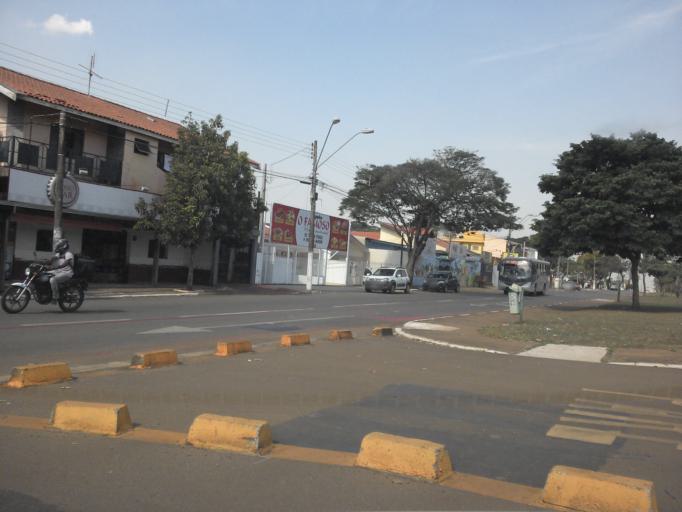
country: BR
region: Sao Paulo
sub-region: Sumare
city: Sumare
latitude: -22.8295
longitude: -47.2665
